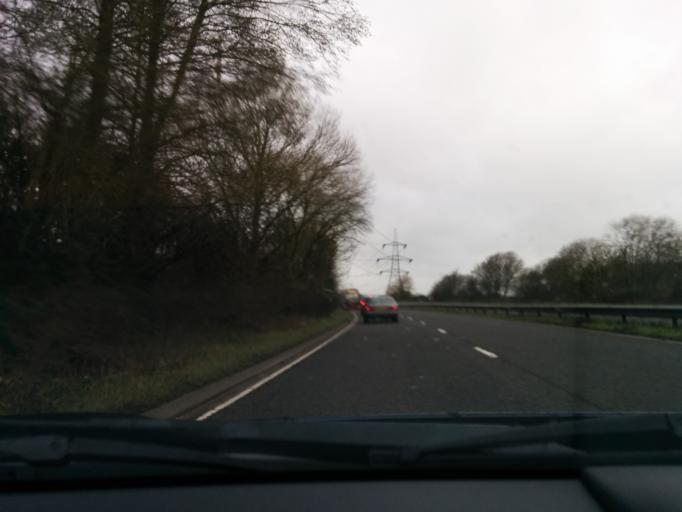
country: GB
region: England
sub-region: Oxfordshire
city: Boars Hill
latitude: 51.7536
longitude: -1.3106
